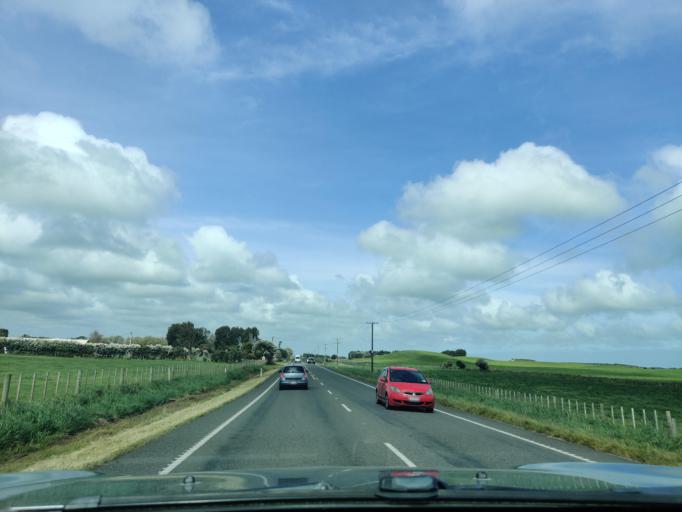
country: NZ
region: Taranaki
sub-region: South Taranaki District
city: Patea
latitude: -39.7713
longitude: 174.6699
